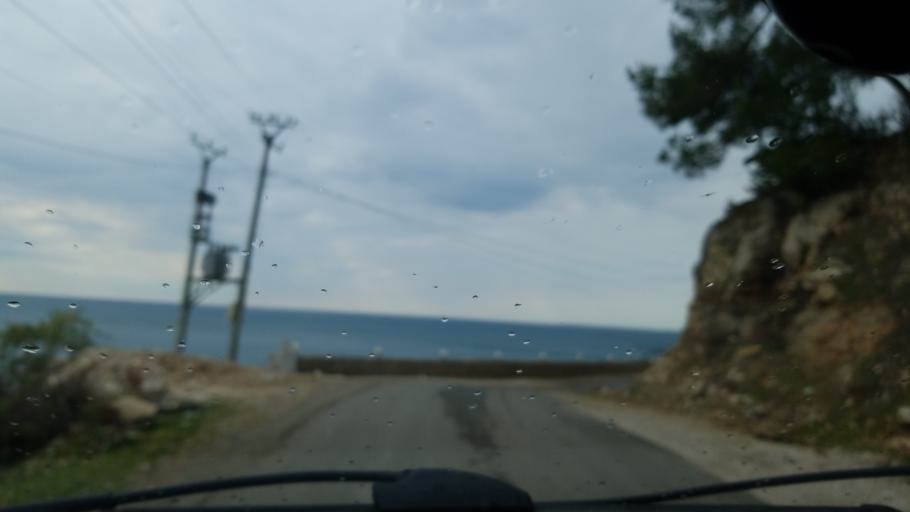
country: AL
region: Lezhe
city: Shengjin
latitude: 41.8147
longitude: 19.5703
